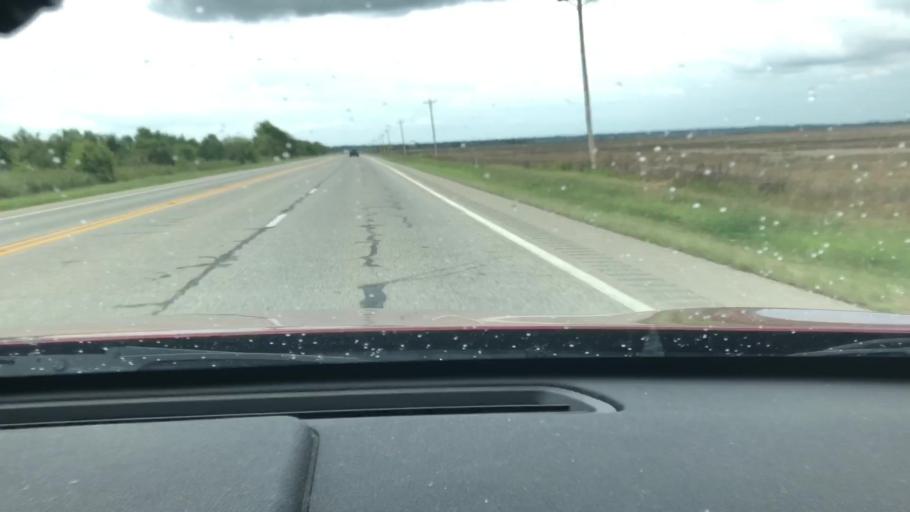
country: US
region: Arkansas
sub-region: Lafayette County
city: Lewisville
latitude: 33.4120
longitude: -93.7781
